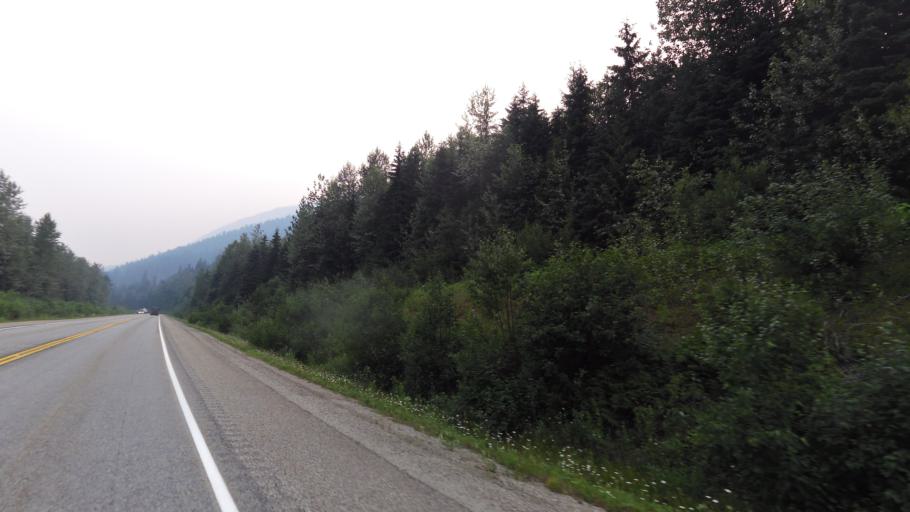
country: CA
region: Alberta
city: Jasper Park Lodge
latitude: 52.3272
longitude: -119.1769
